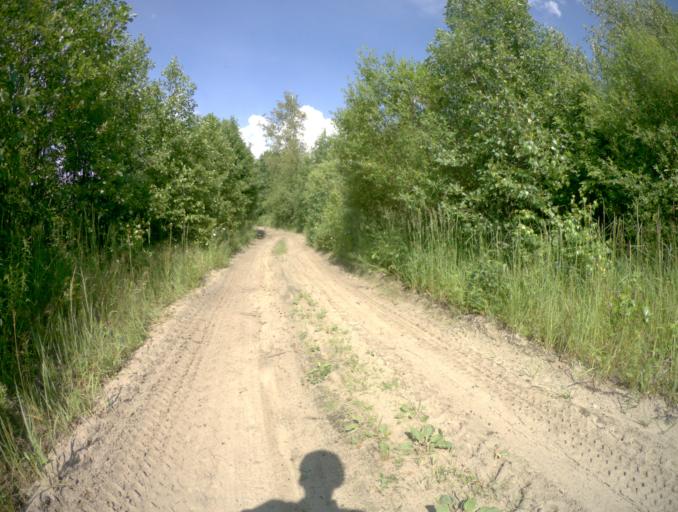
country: RU
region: Ivanovo
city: Talitsy
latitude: 56.5347
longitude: 42.2493
